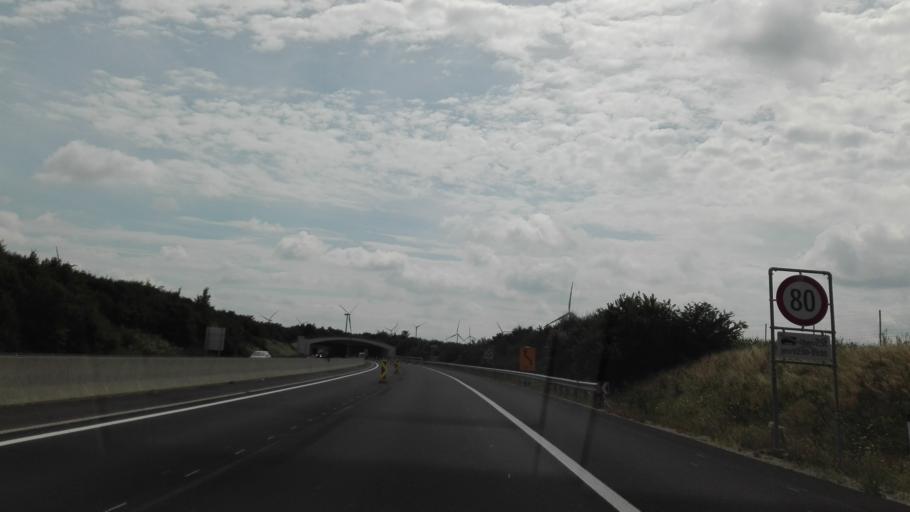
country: AT
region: Burgenland
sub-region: Politischer Bezirk Neusiedl am See
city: Gols
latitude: 47.9448
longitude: 16.9389
